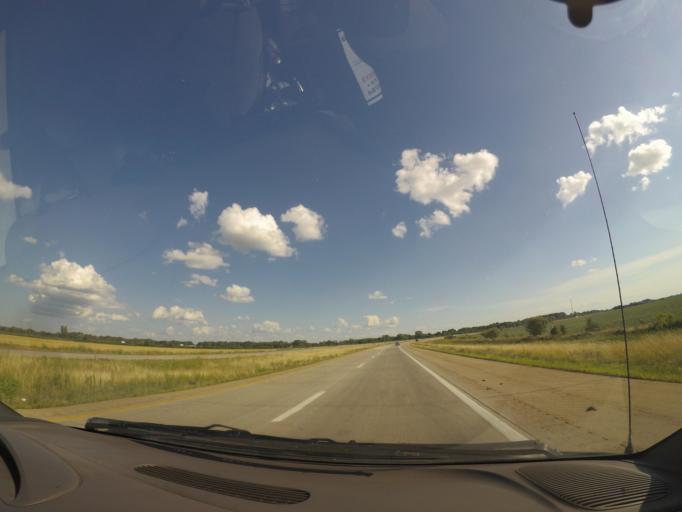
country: US
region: Ohio
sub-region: Lucas County
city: Whitehouse
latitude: 41.4733
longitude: -83.7765
